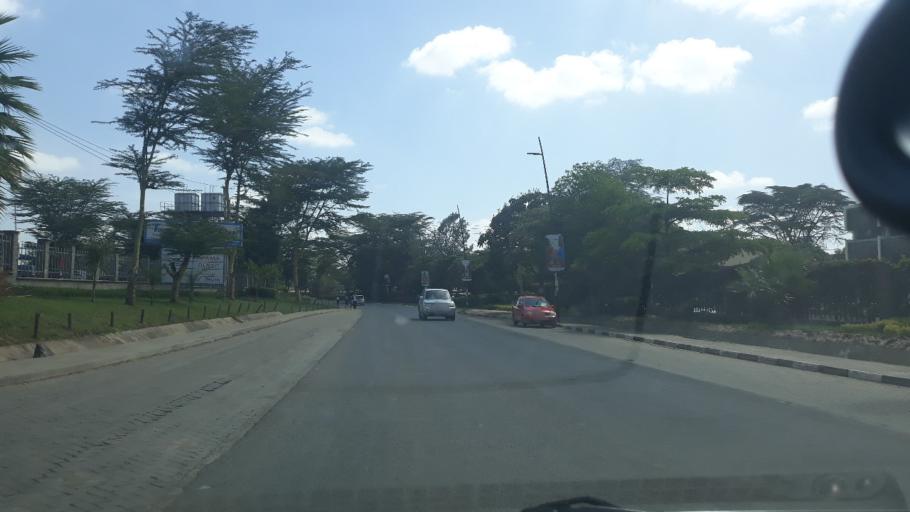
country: KE
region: Nairobi Area
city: Pumwani
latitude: -1.3220
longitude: 36.8345
